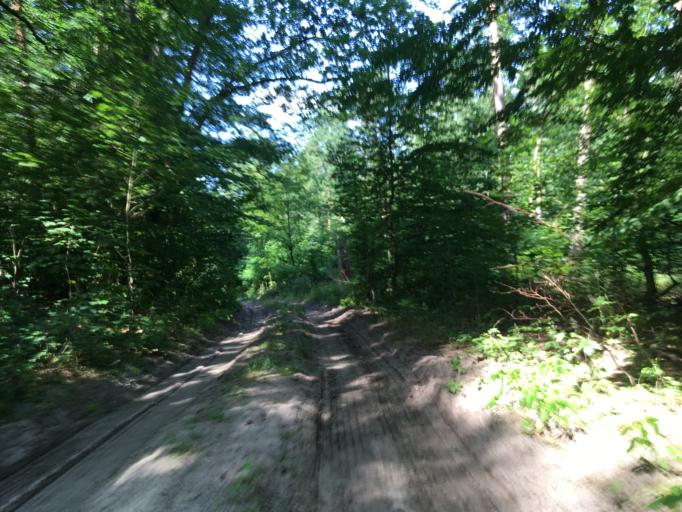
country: DE
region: Brandenburg
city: Casekow
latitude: 53.2308
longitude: 14.1296
